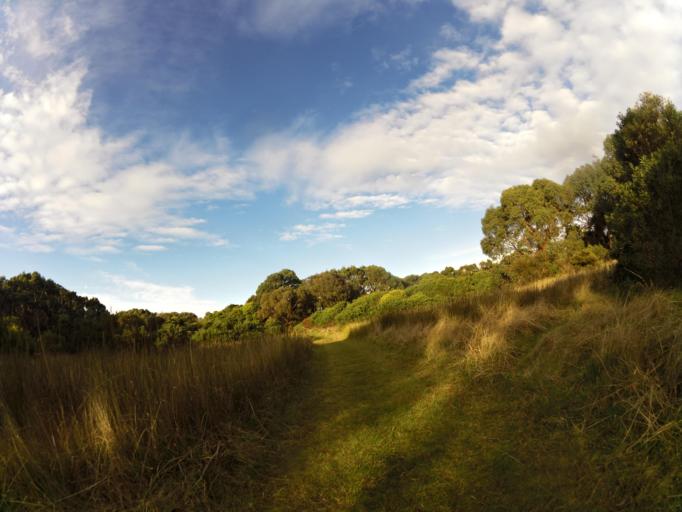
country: AU
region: Victoria
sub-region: Bass Coast
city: North Wonthaggi
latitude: -38.6031
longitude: 145.5624
